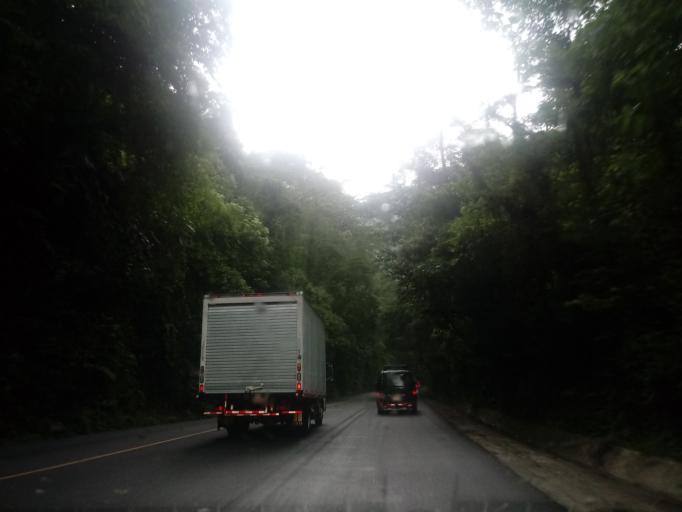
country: CR
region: San Jose
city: Dulce Nombre de Jesus
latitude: 10.1471
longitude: -83.9535
